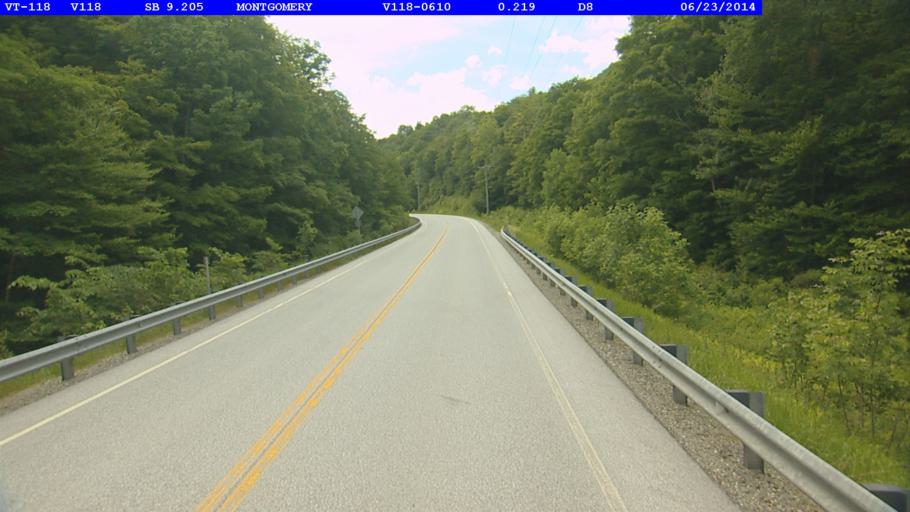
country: US
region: Vermont
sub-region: Lamoille County
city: Johnson
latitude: 44.8038
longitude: -72.6241
